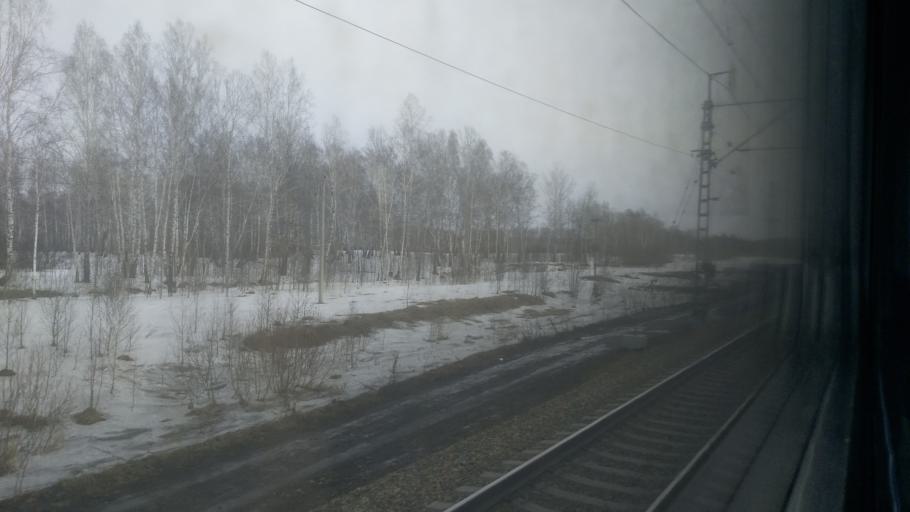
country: RU
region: Novosibirsk
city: Stantsionno-Oyashinskiy
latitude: 55.5069
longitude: 83.9263
